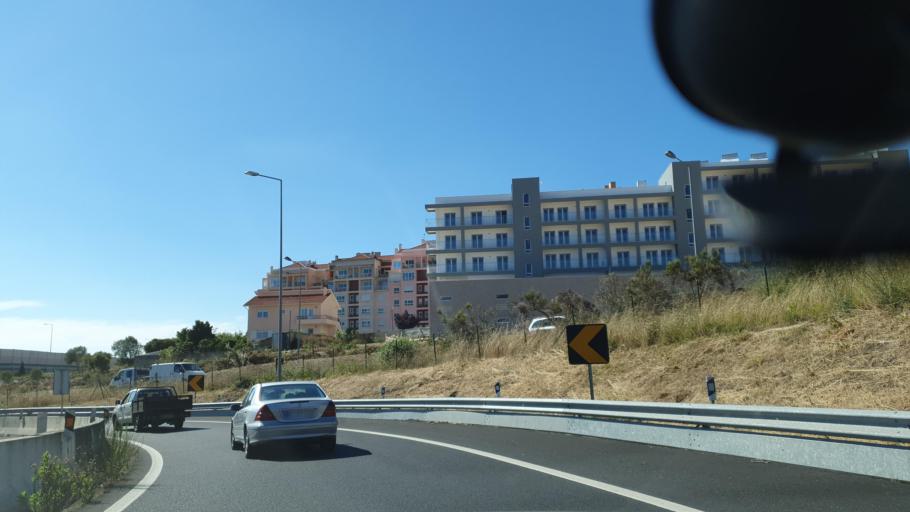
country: PT
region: Lisbon
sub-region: Sintra
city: Belas
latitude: 38.7750
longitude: -9.2801
